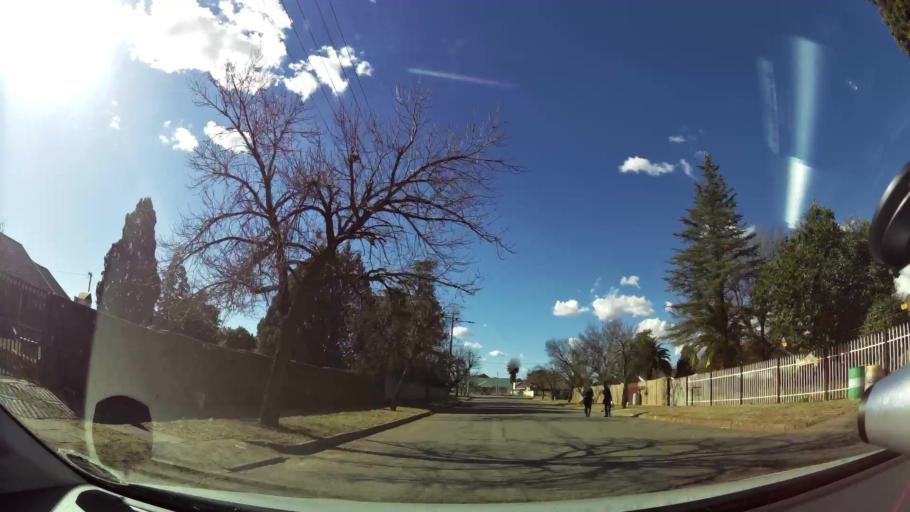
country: ZA
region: North-West
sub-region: Dr Kenneth Kaunda District Municipality
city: Klerksdorp
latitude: -26.8436
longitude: 26.6545
